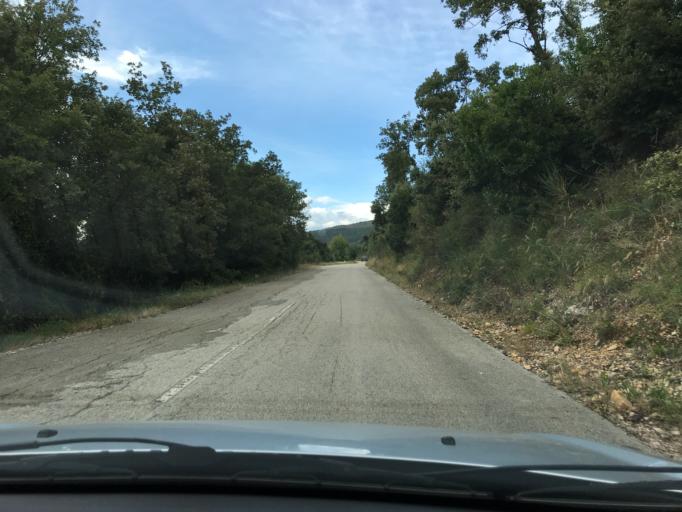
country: IT
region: Umbria
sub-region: Provincia di Terni
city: Montecchio
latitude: 42.6729
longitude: 12.2949
